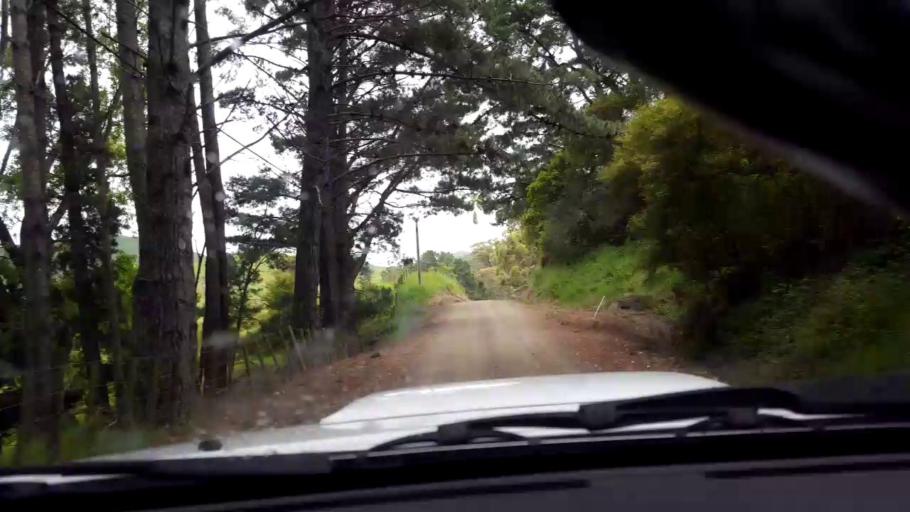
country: NZ
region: Gisborne
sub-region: Gisborne District
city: Gisborne
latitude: -38.3862
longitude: 177.6332
